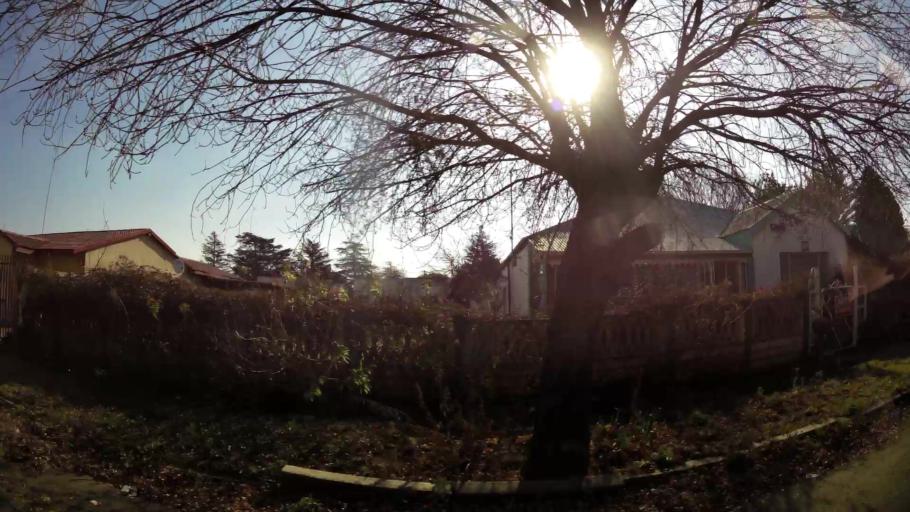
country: ZA
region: Gauteng
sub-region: West Rand District Municipality
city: Randfontein
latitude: -26.1679
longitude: 27.7088
